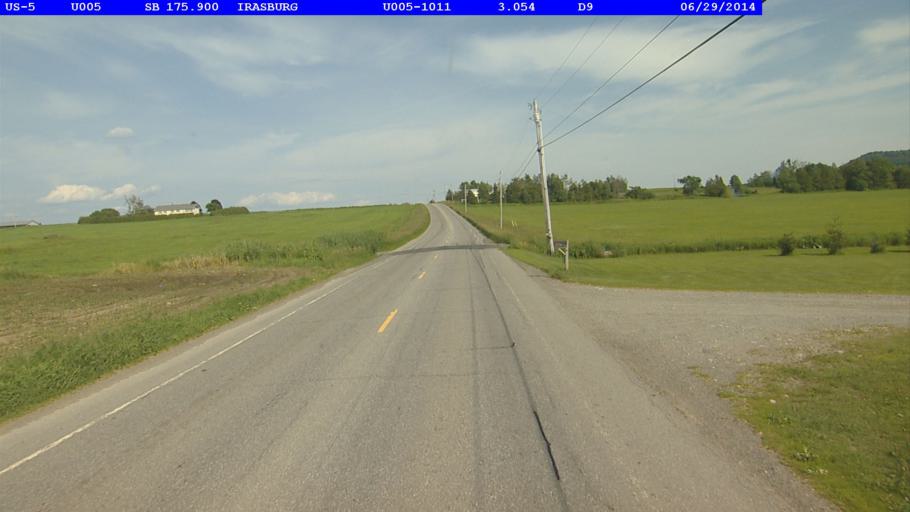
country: US
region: Vermont
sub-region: Orleans County
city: Newport
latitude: 44.8371
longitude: -72.2562
